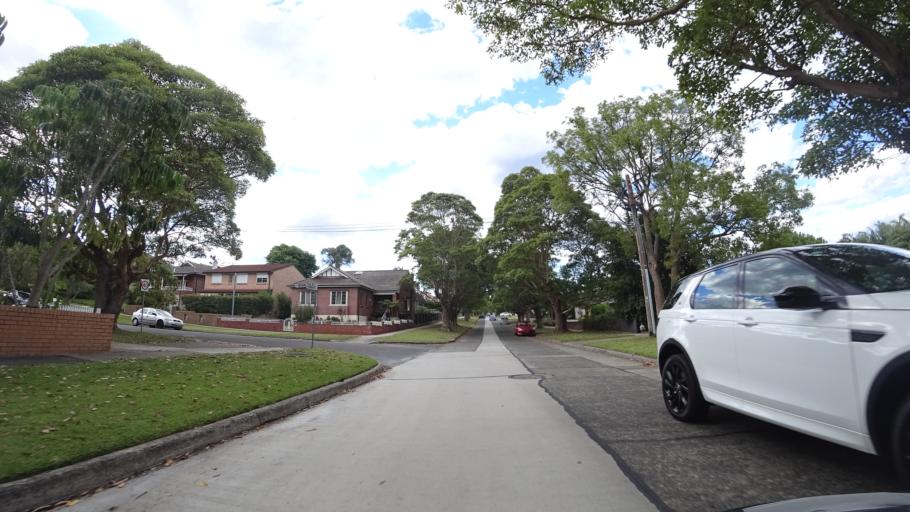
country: AU
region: New South Wales
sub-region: Willoughby
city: Chatswood
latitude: -33.7907
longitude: 151.1908
